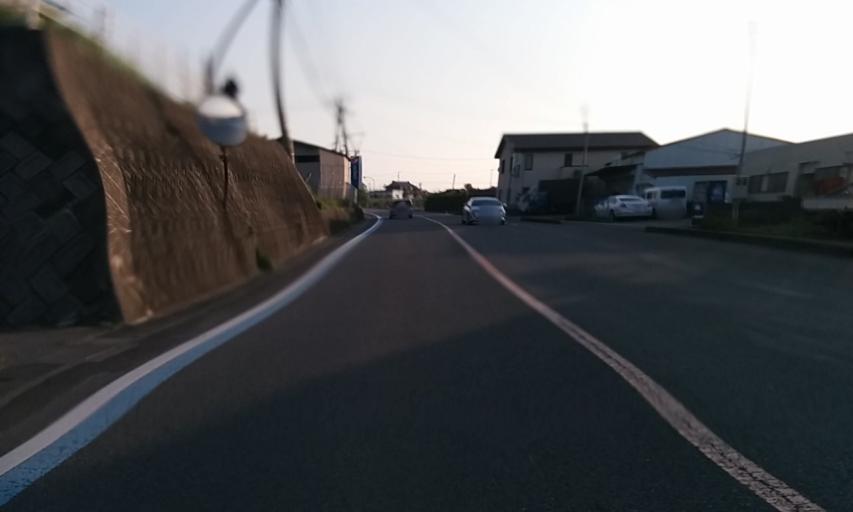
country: JP
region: Ehime
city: Masaki-cho
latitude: 33.7846
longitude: 132.7635
